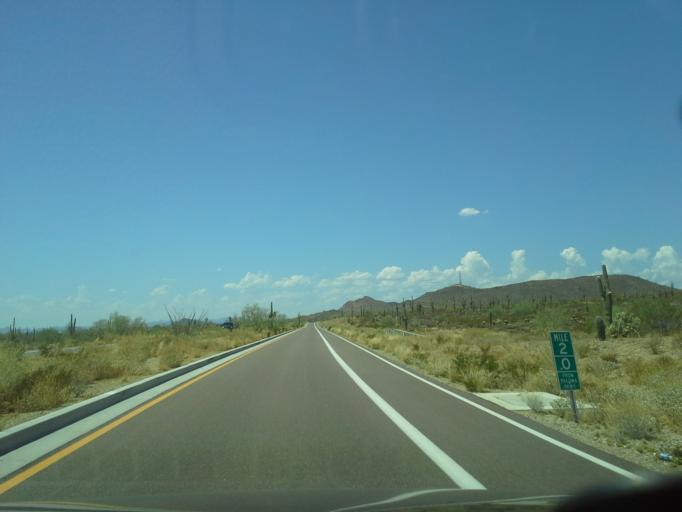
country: US
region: Arizona
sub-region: Maricopa County
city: Anthem
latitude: 33.7746
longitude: -112.0694
